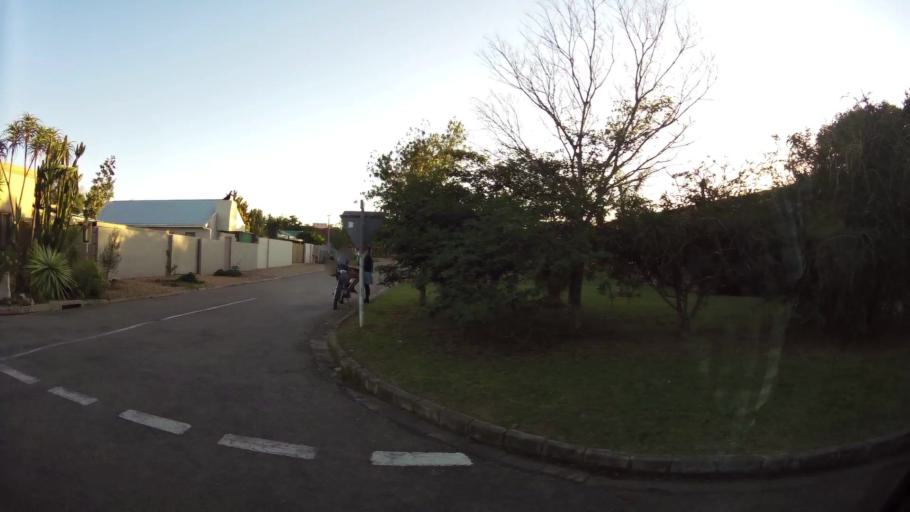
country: ZA
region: Western Cape
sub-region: Eden District Municipality
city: Riversdale
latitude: -34.0840
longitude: 21.2466
